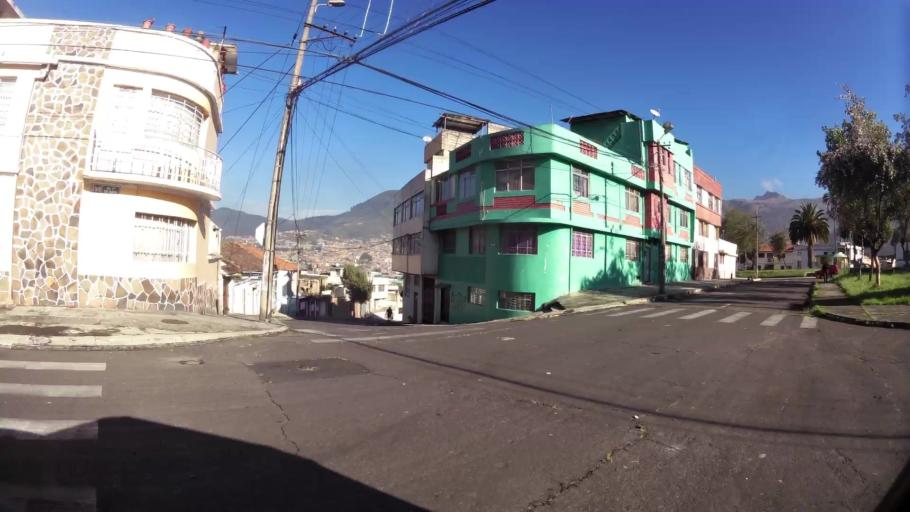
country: EC
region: Pichincha
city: Quito
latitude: -0.2443
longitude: -78.5160
